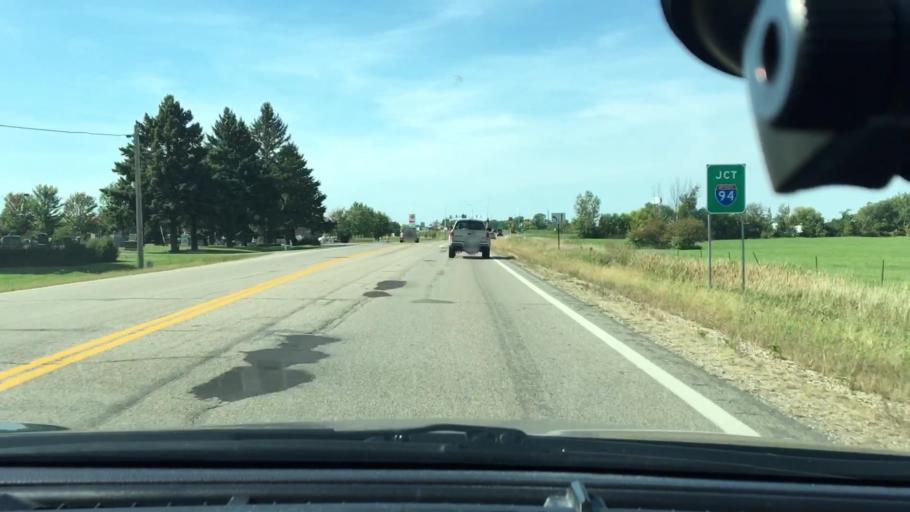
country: US
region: Minnesota
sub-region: Wright County
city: Albertville
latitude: 45.2380
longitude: -93.6421
